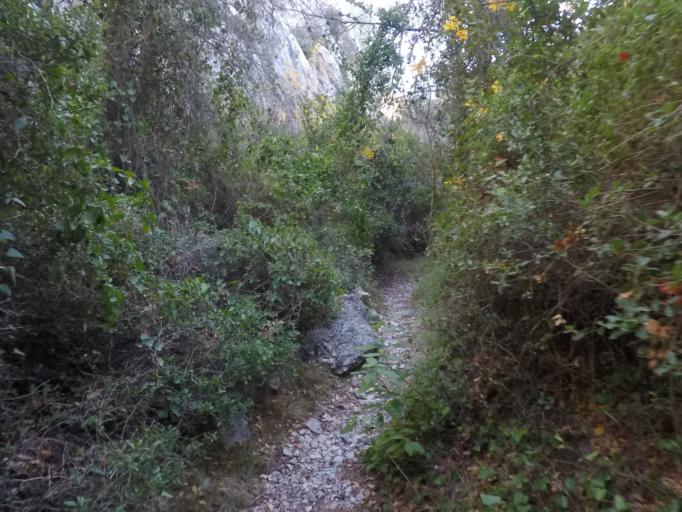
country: FR
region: Provence-Alpes-Cote d'Azur
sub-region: Departement des Bouches-du-Rhone
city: La Penne-sur-Huveaune
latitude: 43.2691
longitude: 5.5025
